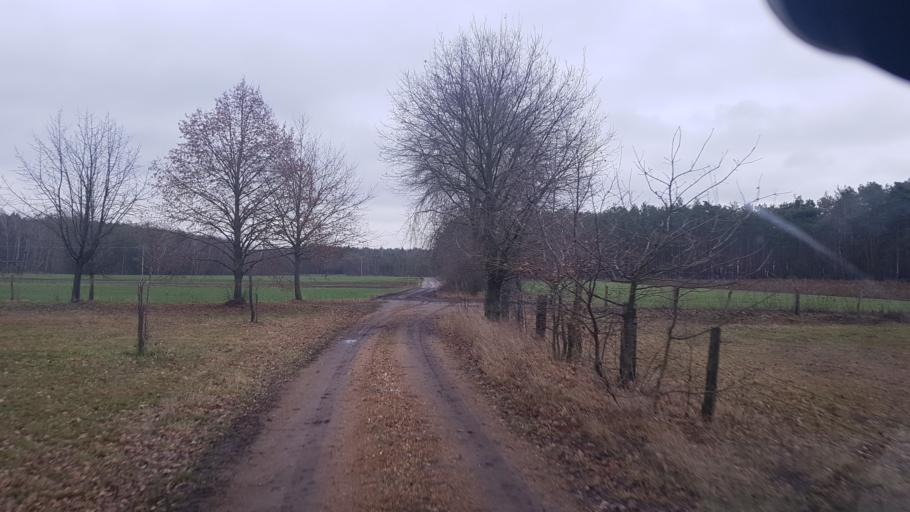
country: DE
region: Brandenburg
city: Ruckersdorf
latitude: 51.6023
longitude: 13.5925
